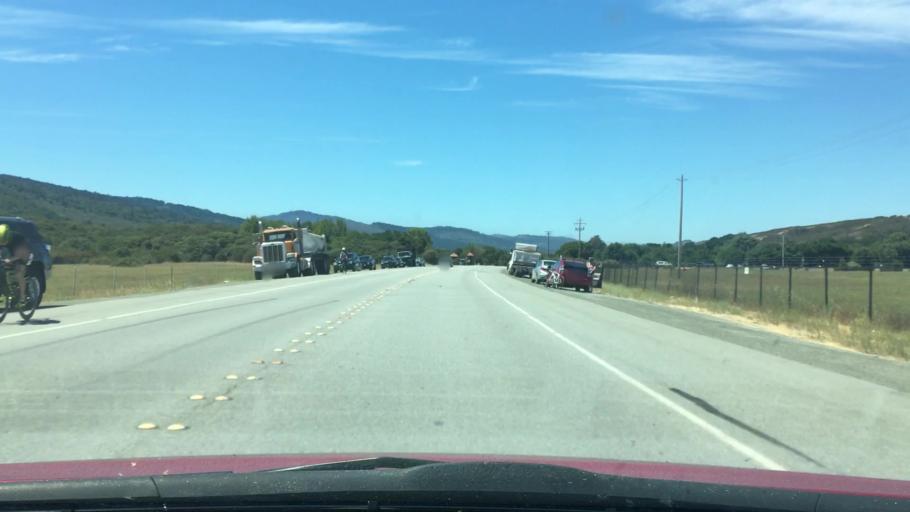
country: US
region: California
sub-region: San Mateo County
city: Emerald Lake Hills
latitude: 37.4621
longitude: -122.2959
